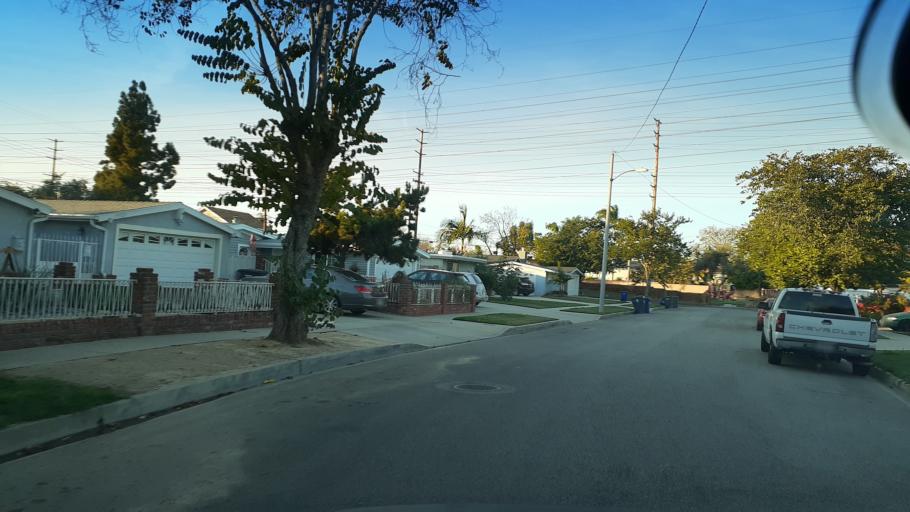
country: US
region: California
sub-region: Los Angeles County
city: Artesia
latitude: 33.8488
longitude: -118.0834
